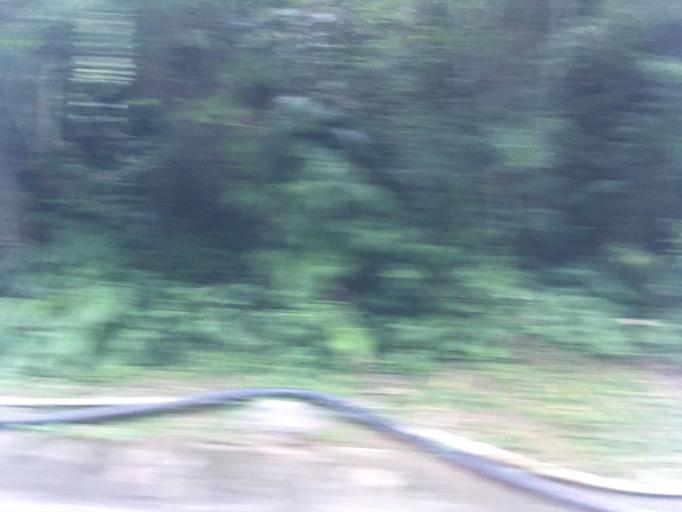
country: TW
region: Taiwan
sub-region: Yilan
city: Yilan
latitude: 24.4371
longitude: 121.7594
